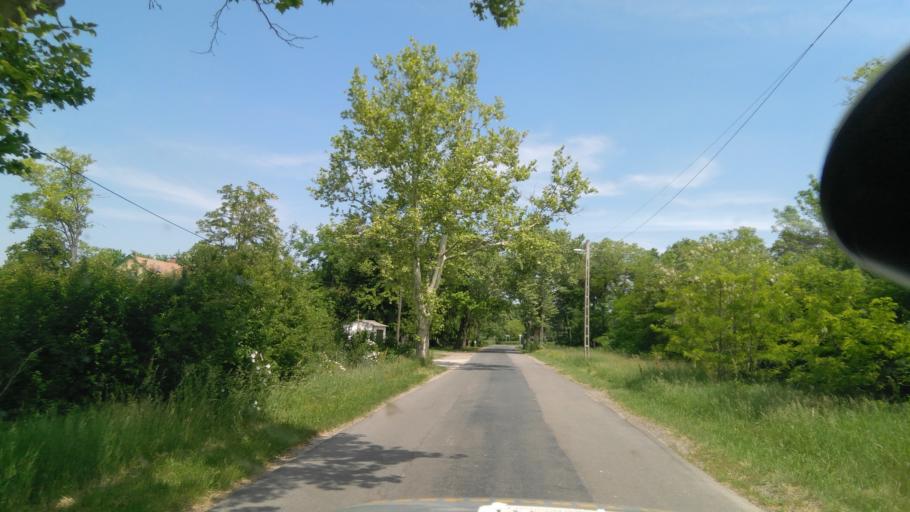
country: HU
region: Csongrad
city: Fabiansebestyen
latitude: 46.5861
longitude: 20.4697
